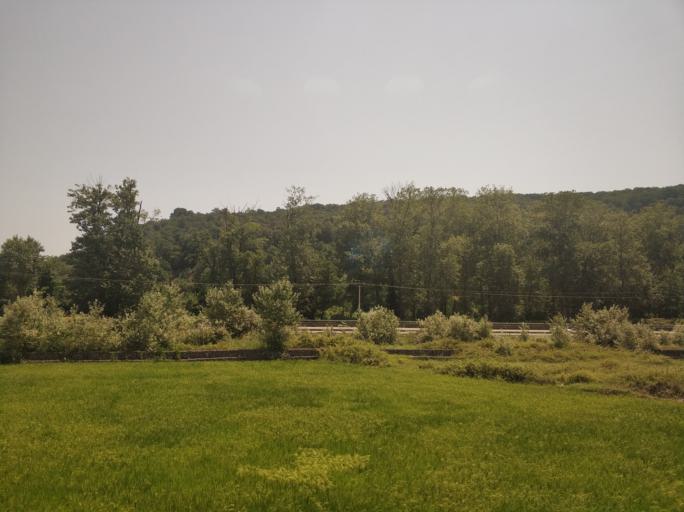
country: IR
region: Gilan
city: Pa'in-e Bazar-e Rudbar
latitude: 36.9594
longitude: 49.5534
